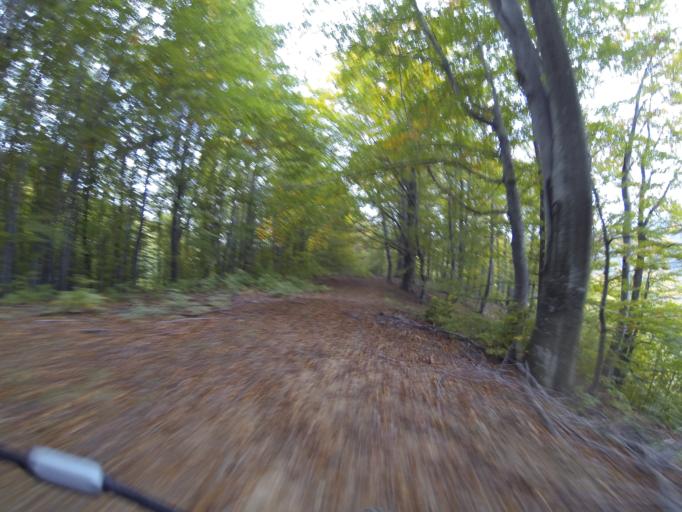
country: RO
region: Gorj
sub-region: Comuna Tismana
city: Sohodol
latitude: 45.0911
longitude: 22.8858
